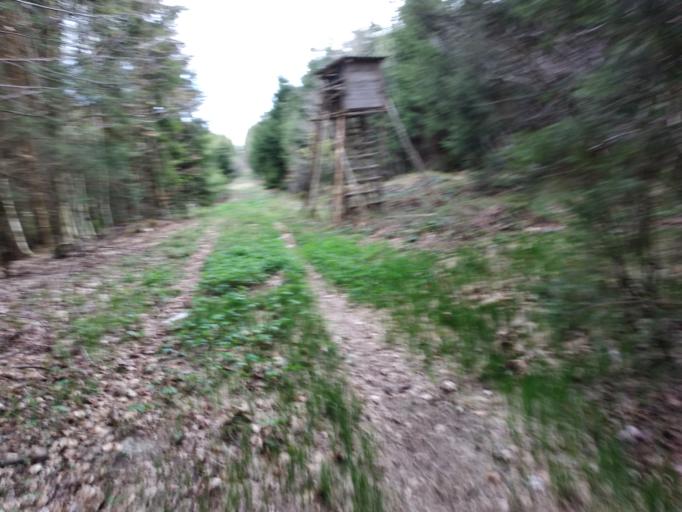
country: DE
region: Bavaria
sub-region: Swabia
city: Lautrach
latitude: 47.8935
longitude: 10.1281
